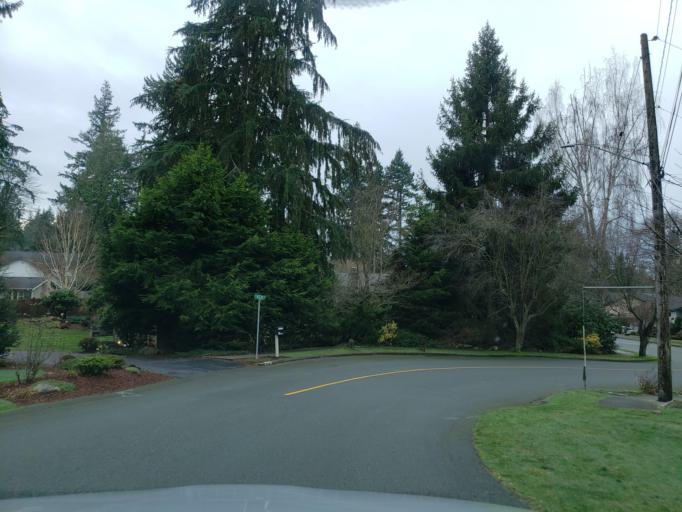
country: US
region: Washington
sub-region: Snohomish County
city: Meadowdale
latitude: 47.8305
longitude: -122.3492
